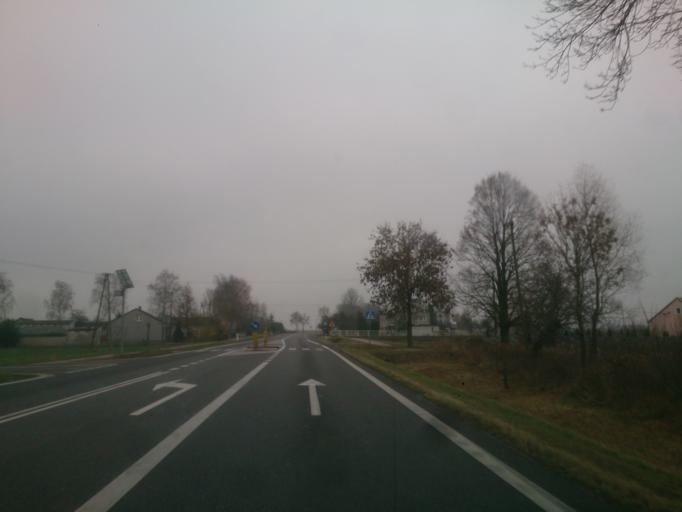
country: PL
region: Masovian Voivodeship
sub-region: Powiat plocki
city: Drobin
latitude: 52.7218
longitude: 20.0155
